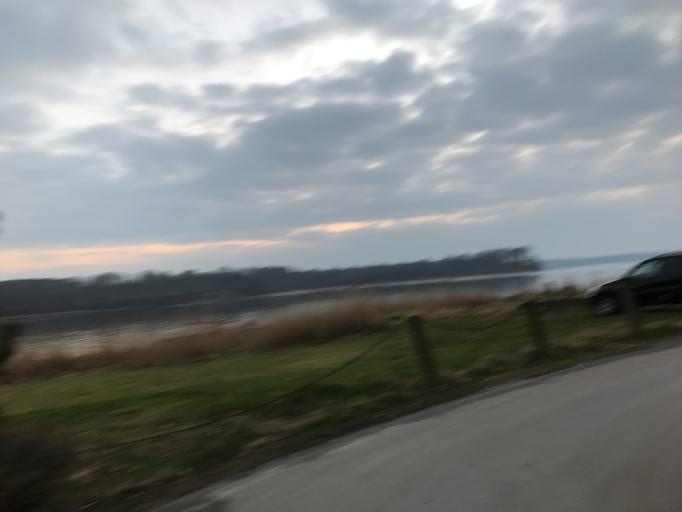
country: DK
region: South Denmark
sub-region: Fredericia Kommune
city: Snoghoj
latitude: 55.5028
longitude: 9.6915
